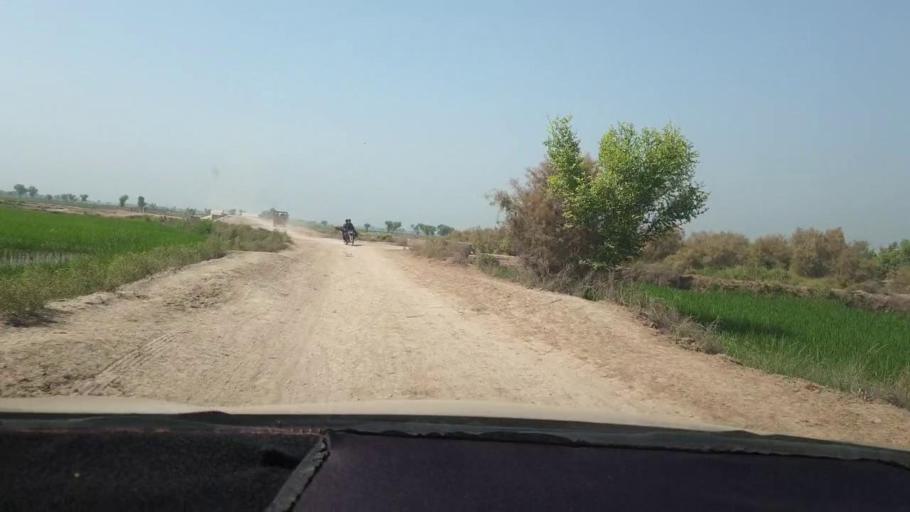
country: PK
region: Sindh
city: Miro Khan
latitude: 27.7158
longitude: 68.0388
